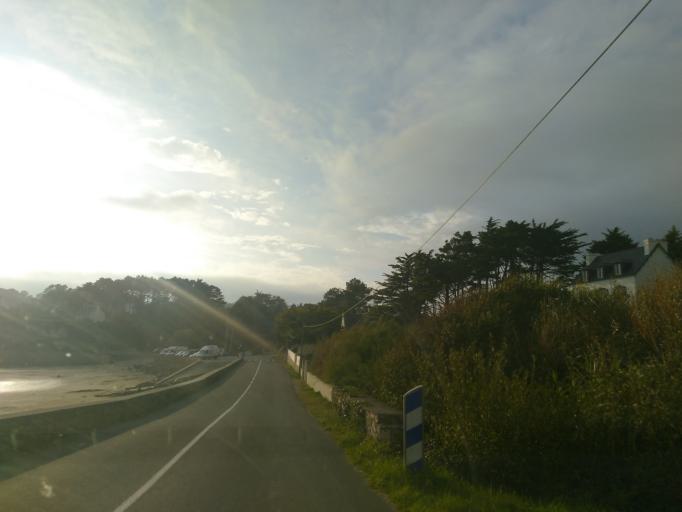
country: FR
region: Brittany
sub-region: Departement du Finistere
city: Crozon
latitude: 48.2390
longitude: -4.4621
